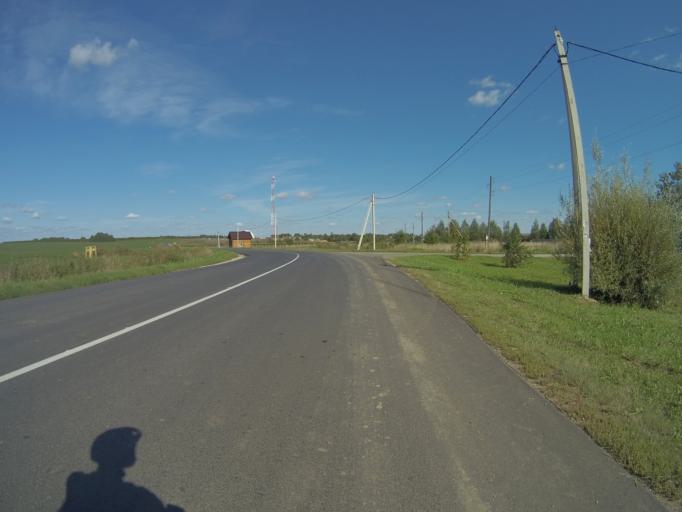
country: RU
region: Vladimir
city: Orgtrud
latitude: 56.3076
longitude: 40.5962
